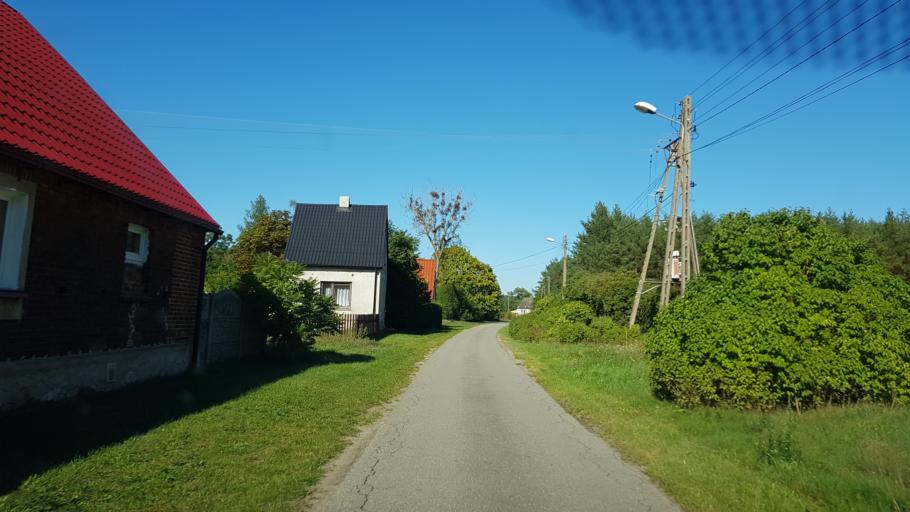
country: PL
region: Lubusz
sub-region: Powiat gorzowski
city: Lubiszyn
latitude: 52.8526
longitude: 14.9372
